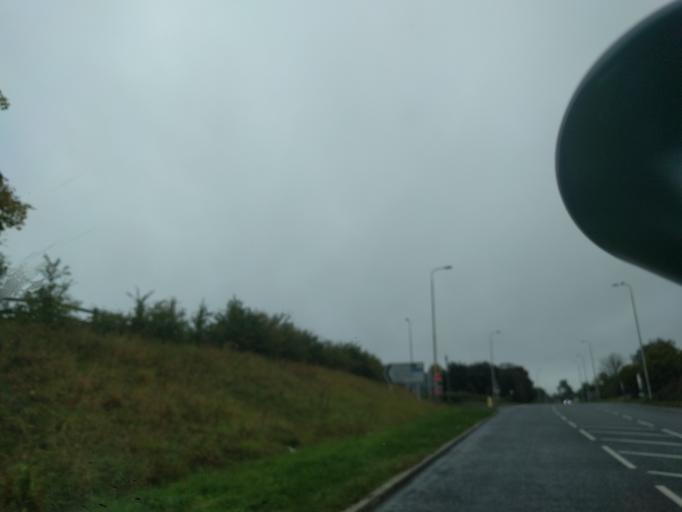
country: GB
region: England
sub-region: North Yorkshire
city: Bedale
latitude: 54.3003
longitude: -1.5678
